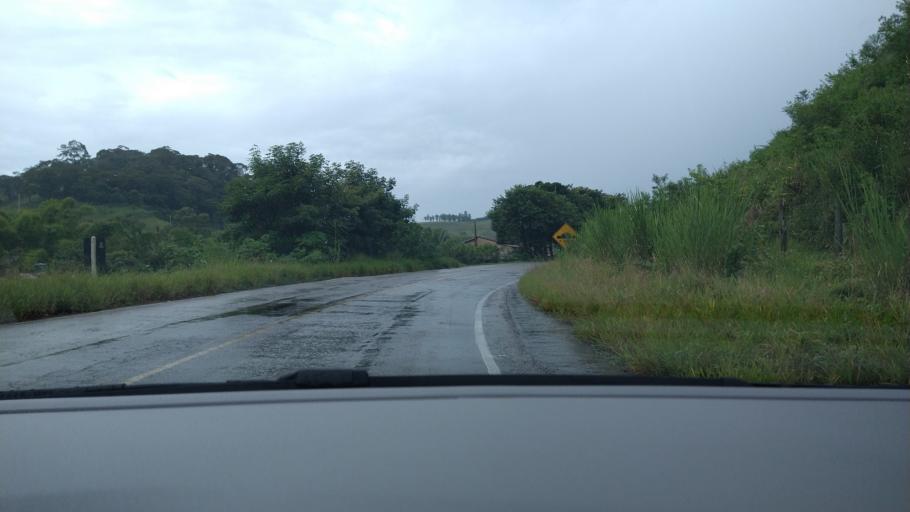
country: BR
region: Minas Gerais
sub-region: Ponte Nova
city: Ponte Nova
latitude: -20.3786
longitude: -42.9015
